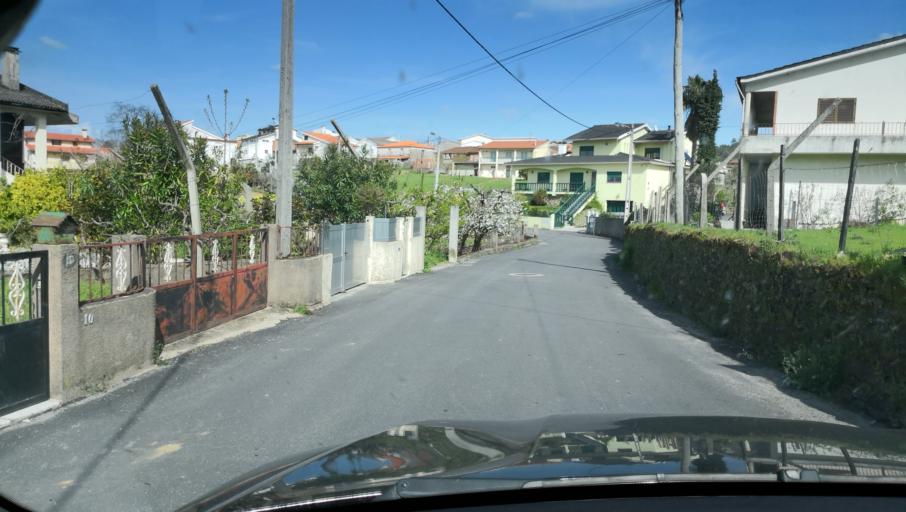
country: PT
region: Vila Real
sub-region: Sabrosa
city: Vilela
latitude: 41.2537
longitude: -7.6682
